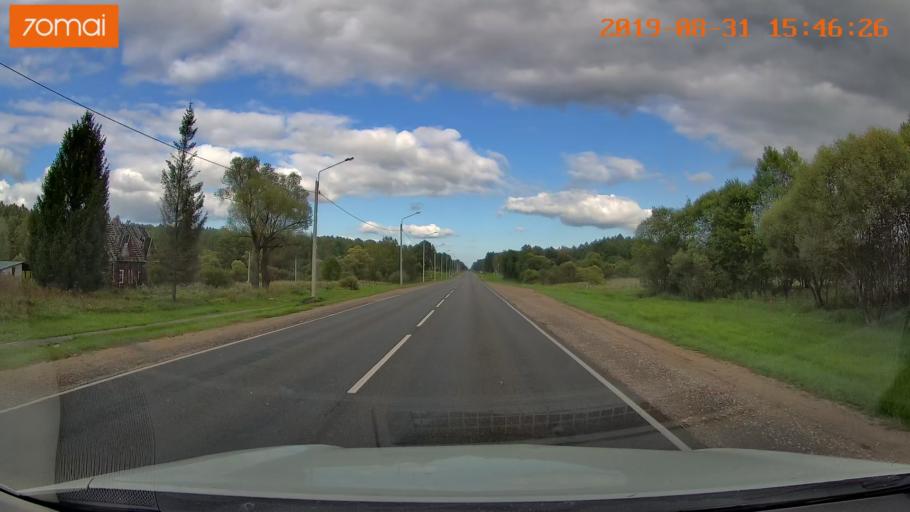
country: RU
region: Kaluga
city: Mosal'sk
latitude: 54.6725
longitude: 34.9821
